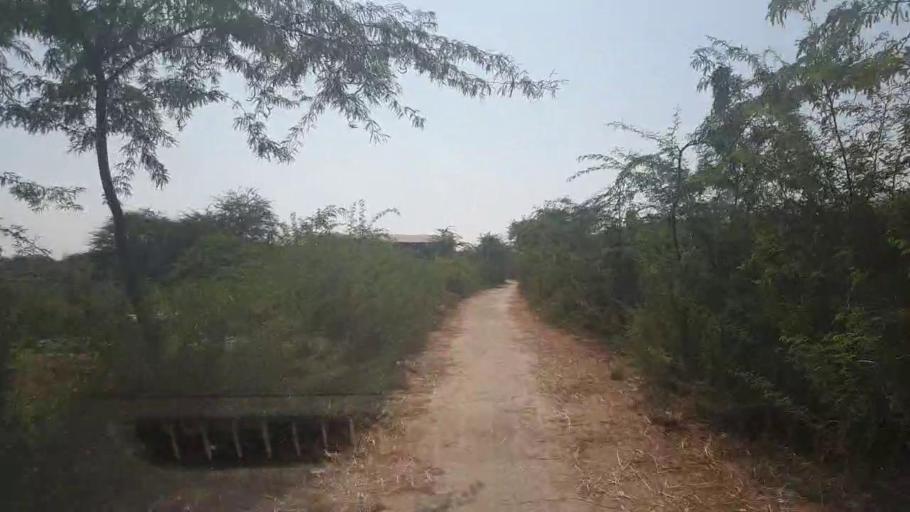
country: PK
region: Sindh
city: Badin
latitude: 24.6288
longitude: 68.9107
